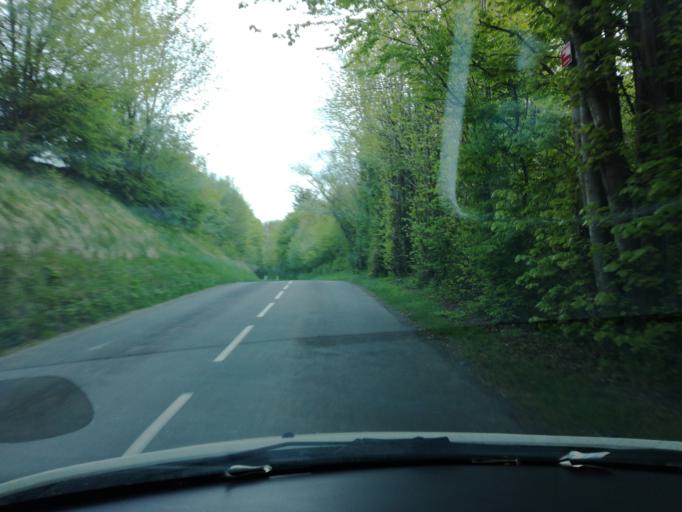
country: FR
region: Picardie
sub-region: Departement de la Somme
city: Poix-de-Picardie
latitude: 49.7824
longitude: 1.9887
